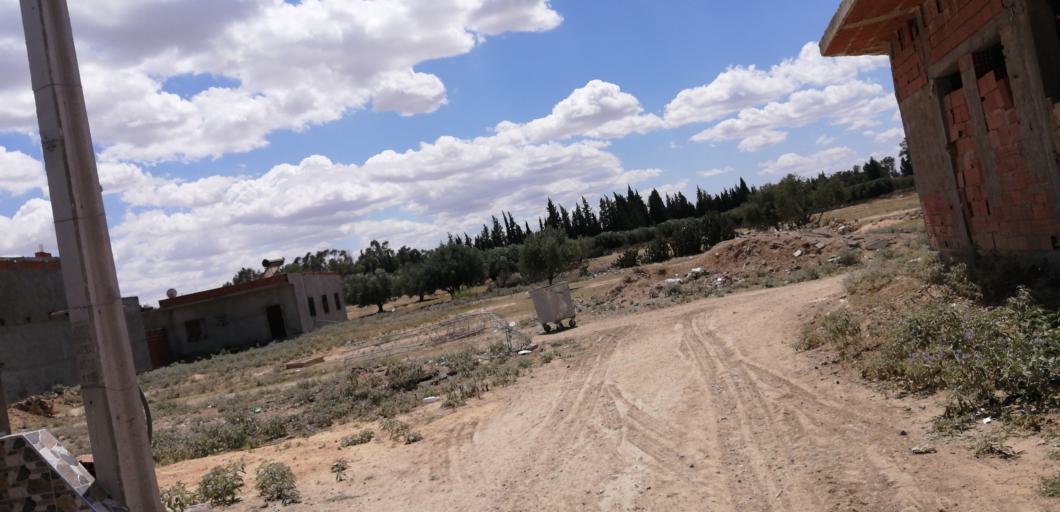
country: TN
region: Al Qayrawan
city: Kairouan
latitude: 35.6165
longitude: 9.9238
